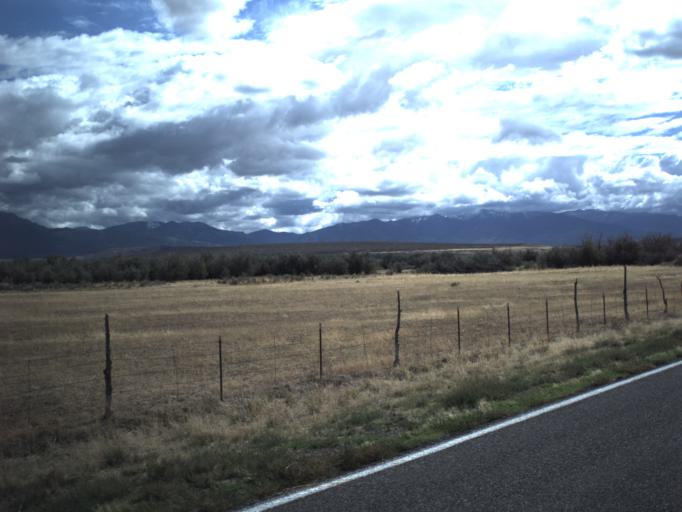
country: US
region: Utah
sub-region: Millard County
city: Fillmore
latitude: 39.0930
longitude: -112.4100
